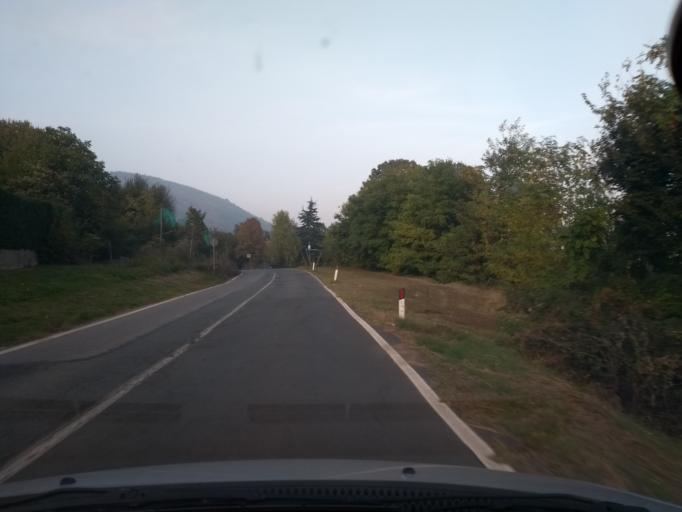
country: IT
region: Piedmont
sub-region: Provincia di Torino
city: Givoletto
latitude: 45.1664
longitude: 7.5026
